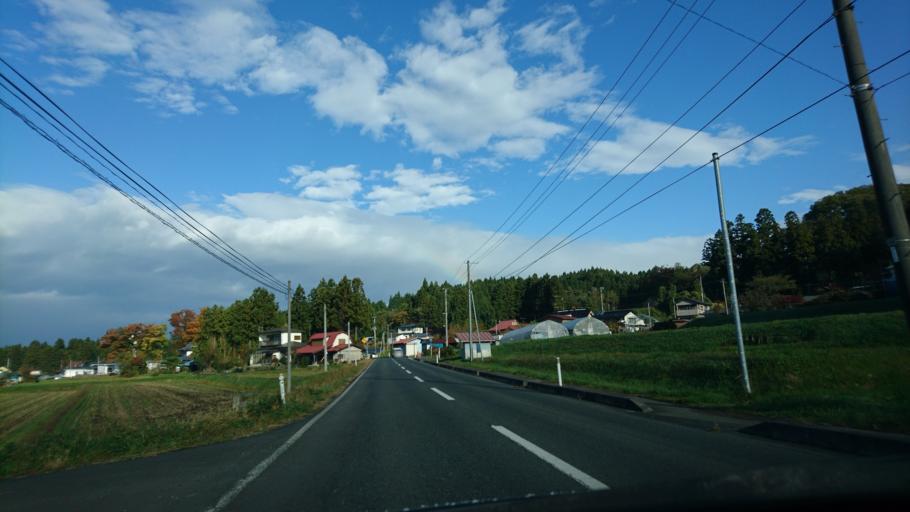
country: JP
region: Iwate
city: Mizusawa
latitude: 39.0323
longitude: 141.0788
